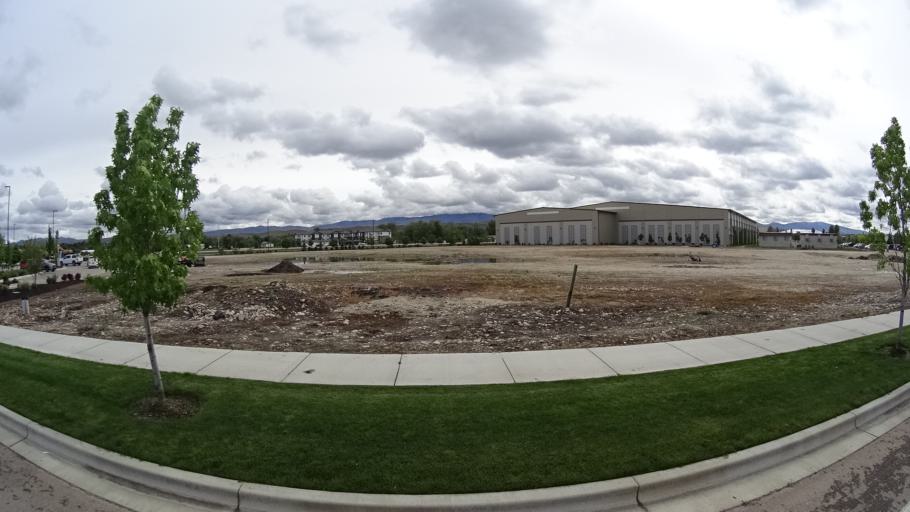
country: US
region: Idaho
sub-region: Ada County
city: Eagle
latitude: 43.6860
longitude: -116.3338
